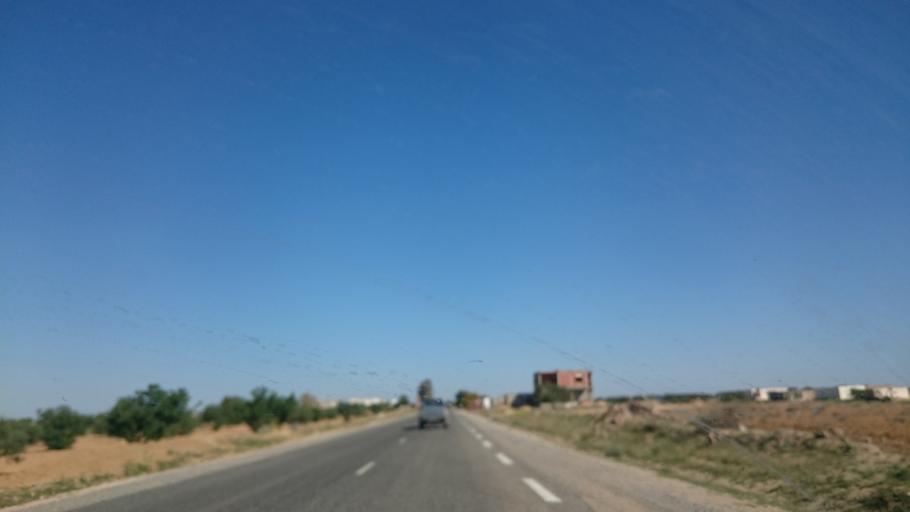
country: TN
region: Safaqis
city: Sfax
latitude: 34.7671
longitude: 10.5110
